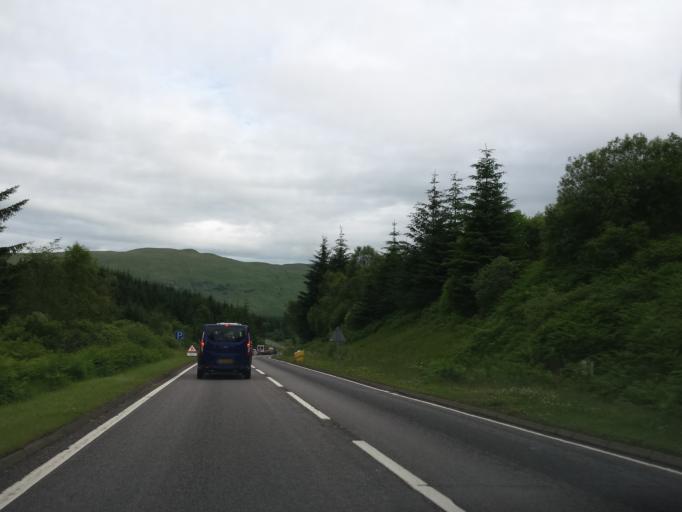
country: GB
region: Scotland
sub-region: Stirling
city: Callander
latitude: 56.4307
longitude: -4.3407
